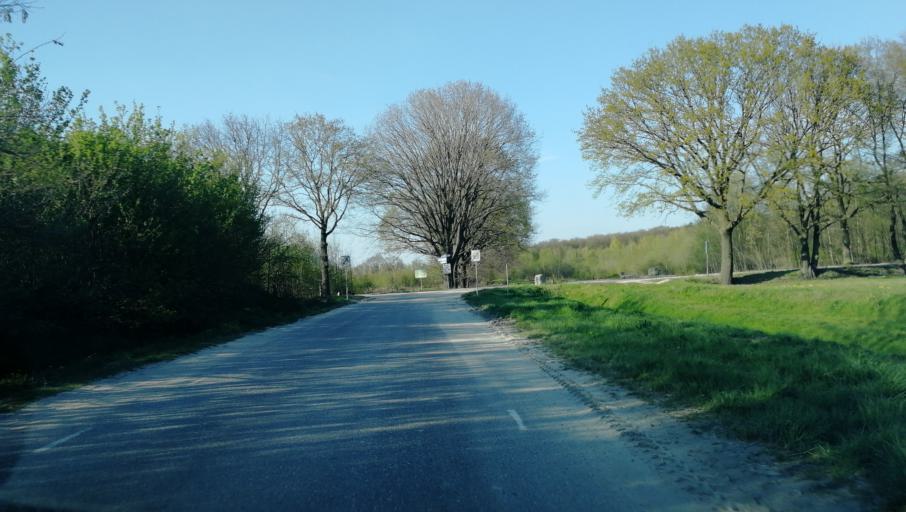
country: NL
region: Limburg
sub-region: Gemeente Venlo
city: Tegelen
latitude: 51.3166
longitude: 6.1399
